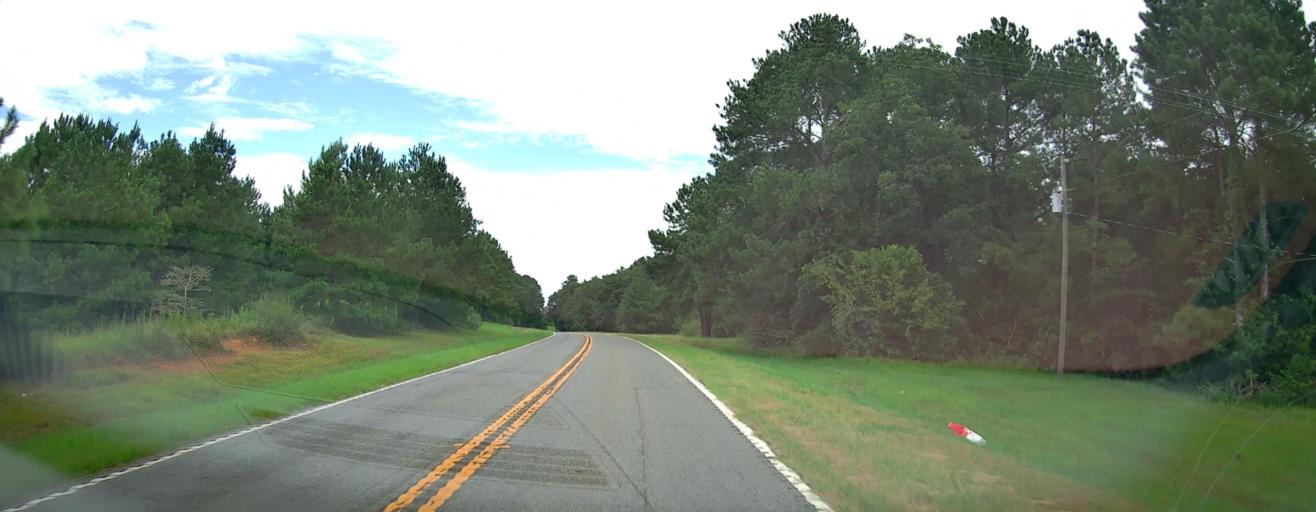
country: US
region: Georgia
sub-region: Dooly County
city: Unadilla
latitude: 32.2814
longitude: -83.8219
